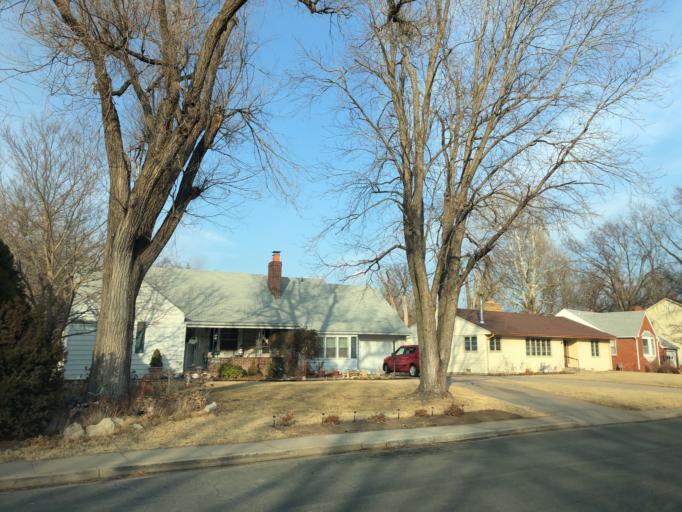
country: US
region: Kansas
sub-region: Reno County
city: Hutchinson
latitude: 38.0766
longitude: -97.9374
